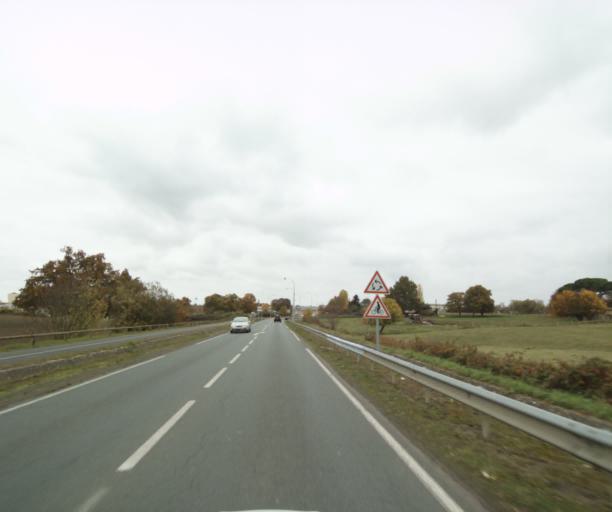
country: FR
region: Poitou-Charentes
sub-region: Departement de la Charente-Maritime
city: Saintes
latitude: 45.7587
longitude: -0.6429
